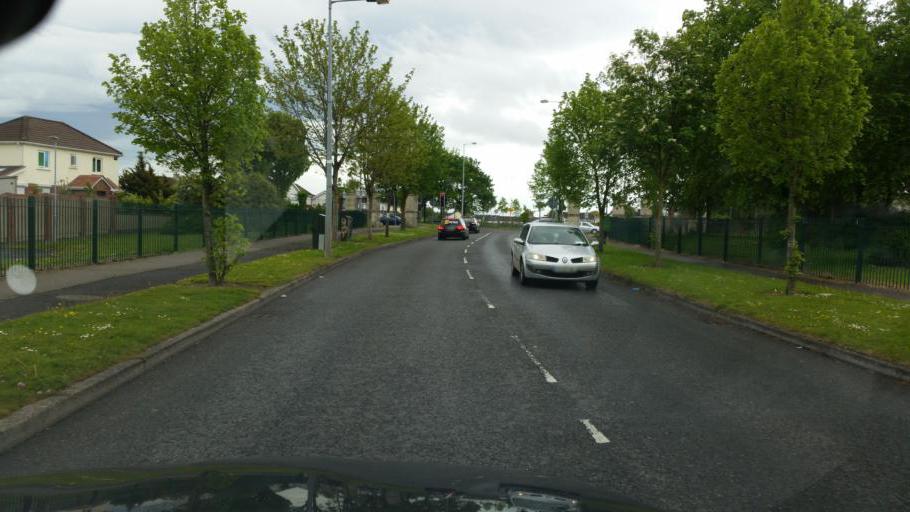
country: IE
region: Leinster
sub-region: Fingal County
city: Blanchardstown
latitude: 53.4003
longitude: -6.3851
